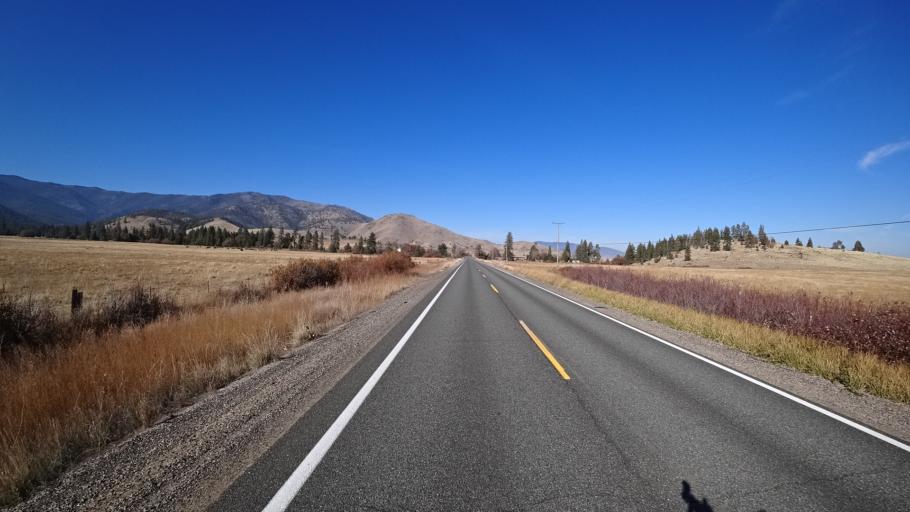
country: US
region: California
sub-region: Siskiyou County
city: Weed
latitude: 41.4459
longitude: -122.4456
